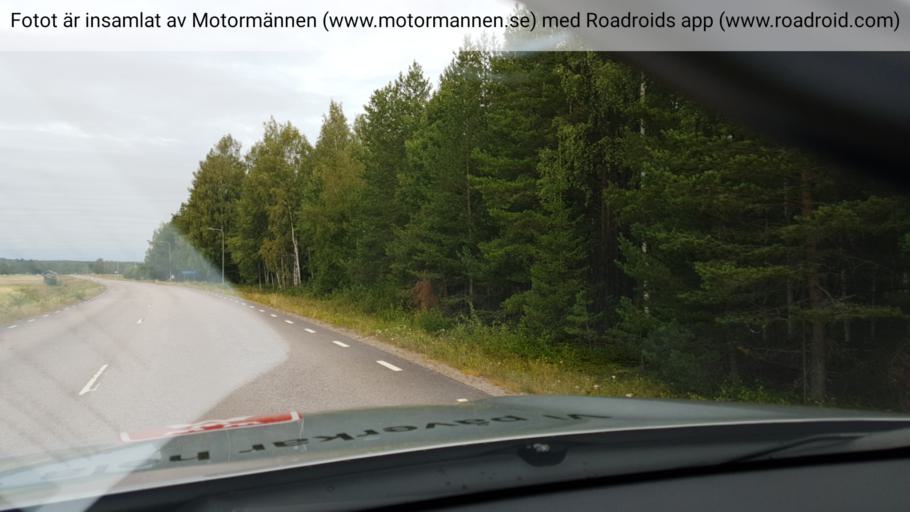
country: SE
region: Norrbotten
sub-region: Lulea Kommun
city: Sodra Sunderbyn
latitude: 65.6485
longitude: 21.8762
